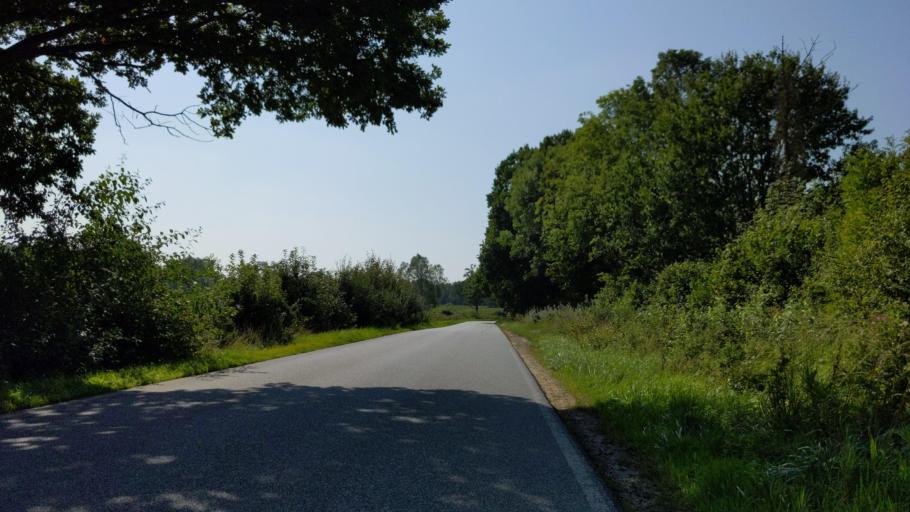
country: DE
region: Schleswig-Holstein
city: Hamberge
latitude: 53.8040
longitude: 10.6062
